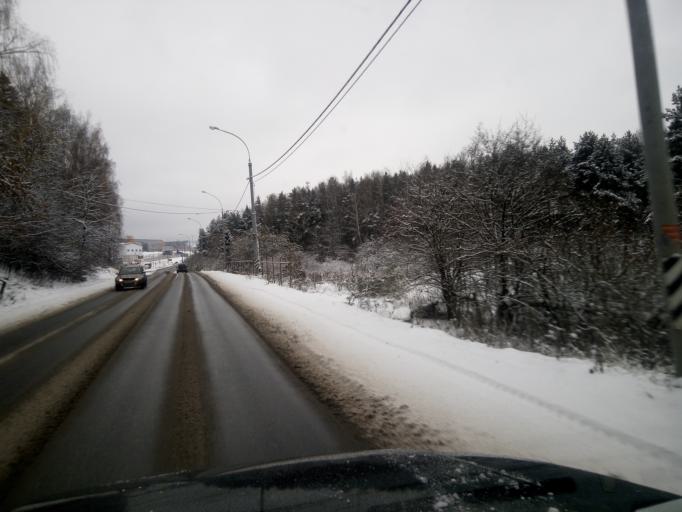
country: RU
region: Moskovskaya
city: Skhodnya
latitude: 55.9660
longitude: 37.3099
